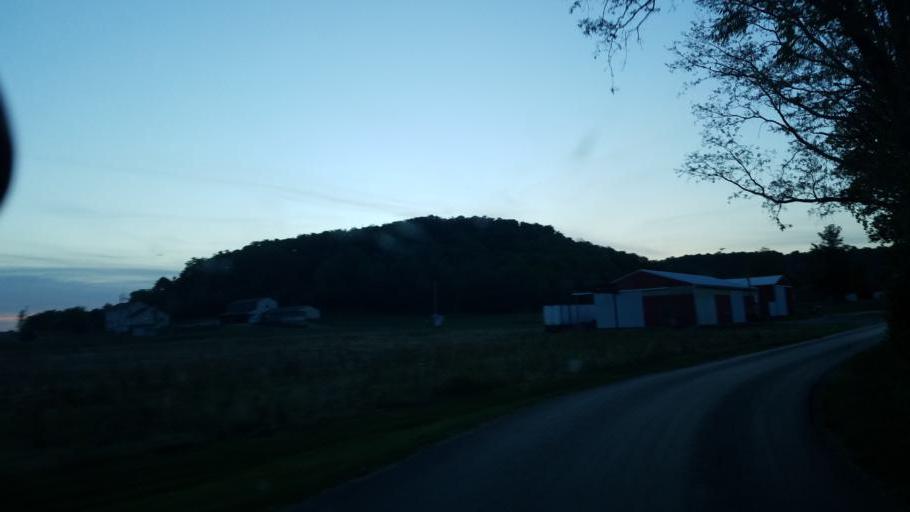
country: US
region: Ohio
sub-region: Highland County
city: Greenfield
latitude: 39.2043
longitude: -83.3529
